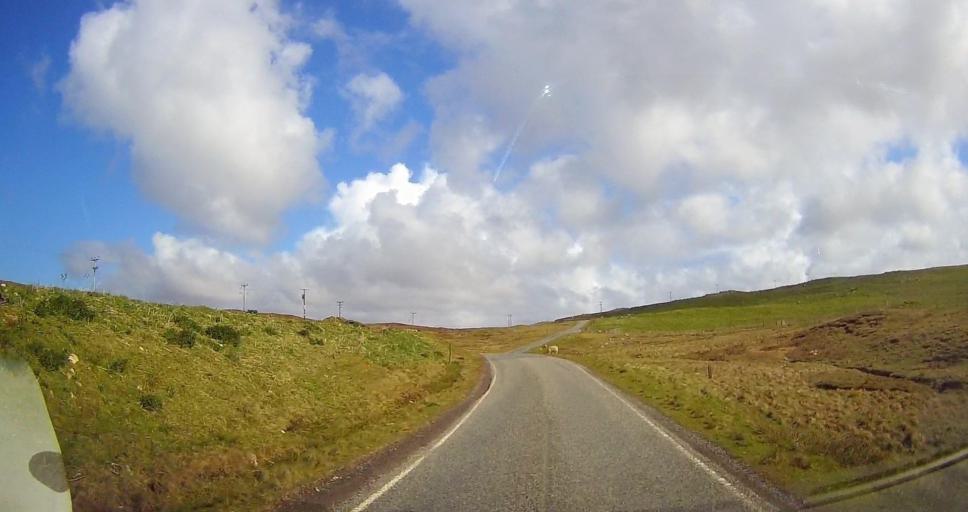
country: GB
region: Scotland
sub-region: Shetland Islands
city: Lerwick
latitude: 60.4782
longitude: -1.4068
